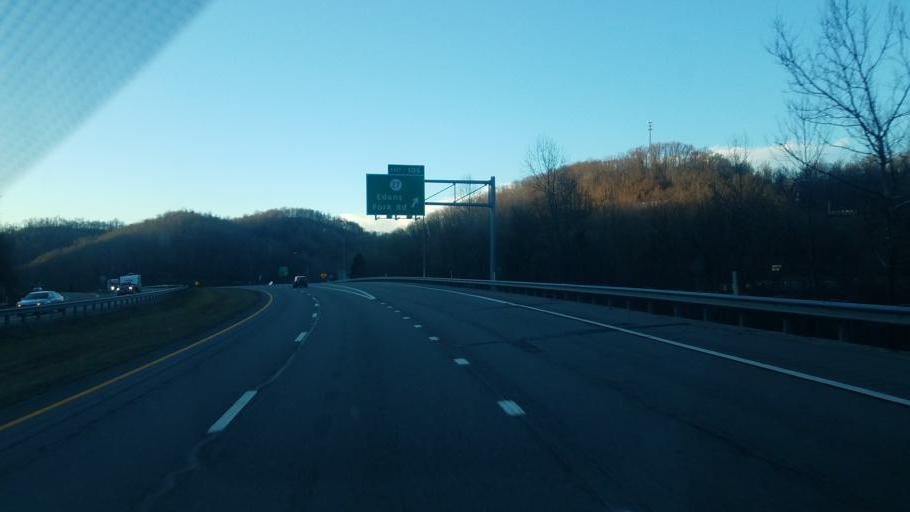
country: US
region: West Virginia
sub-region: Kanawha County
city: Charleston
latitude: 38.4102
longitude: -81.6251
